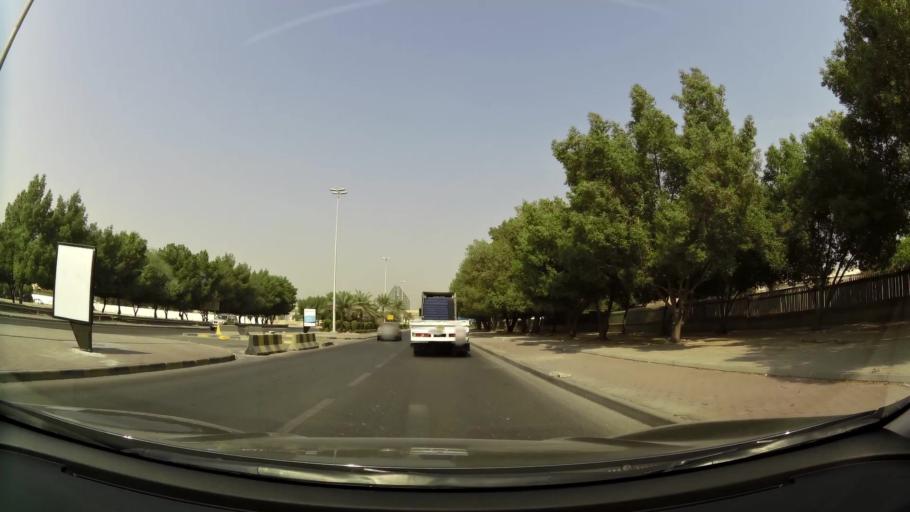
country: KW
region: Al Asimah
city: Ar Rabiyah
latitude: 29.3238
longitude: 47.9223
